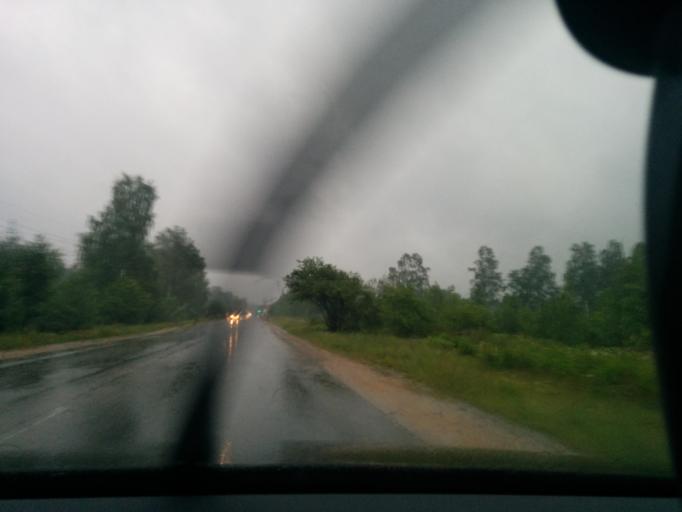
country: LV
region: Stopini
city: Ulbroka
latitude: 56.9142
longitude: 24.2685
